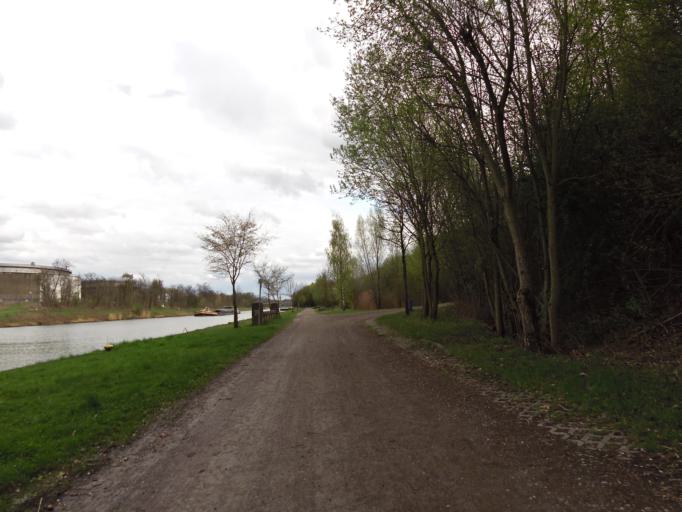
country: DE
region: Lower Saxony
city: Laatzen
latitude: 52.3802
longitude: 9.8415
